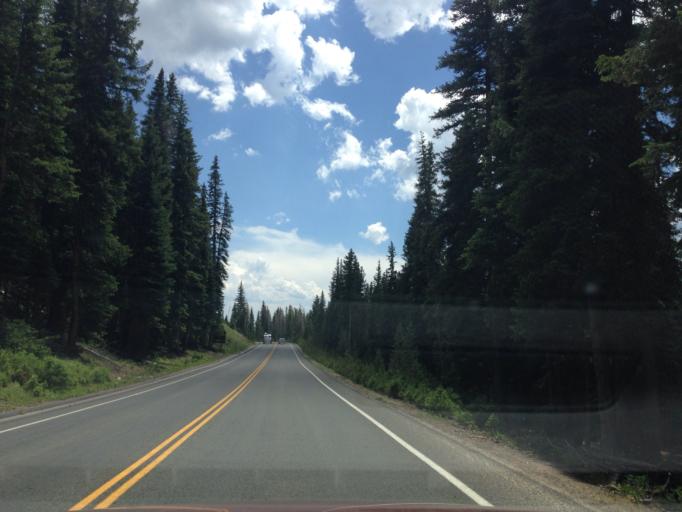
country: US
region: Colorado
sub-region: Grand County
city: Granby
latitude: 40.3455
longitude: -105.8580
